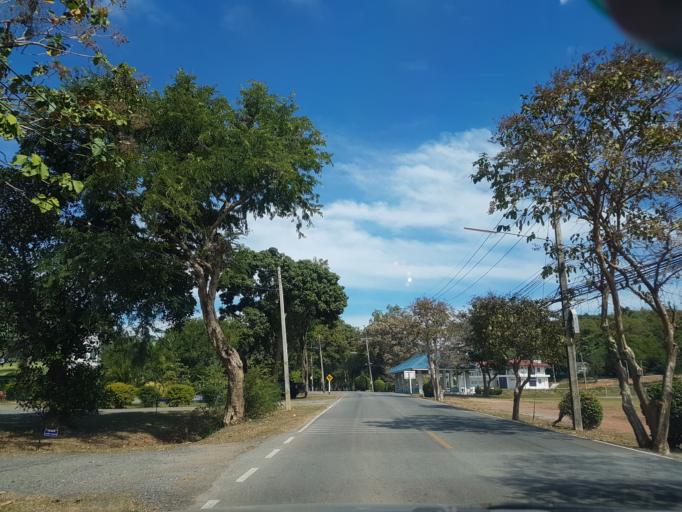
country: TH
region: Chon Buri
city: Sattahip
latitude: 12.6357
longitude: 100.9387
